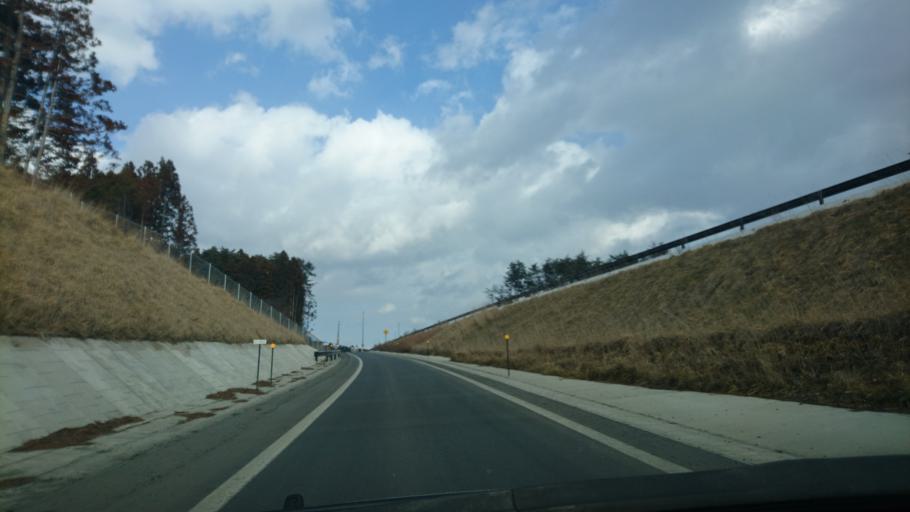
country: JP
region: Miyagi
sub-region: Oshika Gun
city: Onagawa Cho
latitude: 38.6936
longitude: 141.4630
